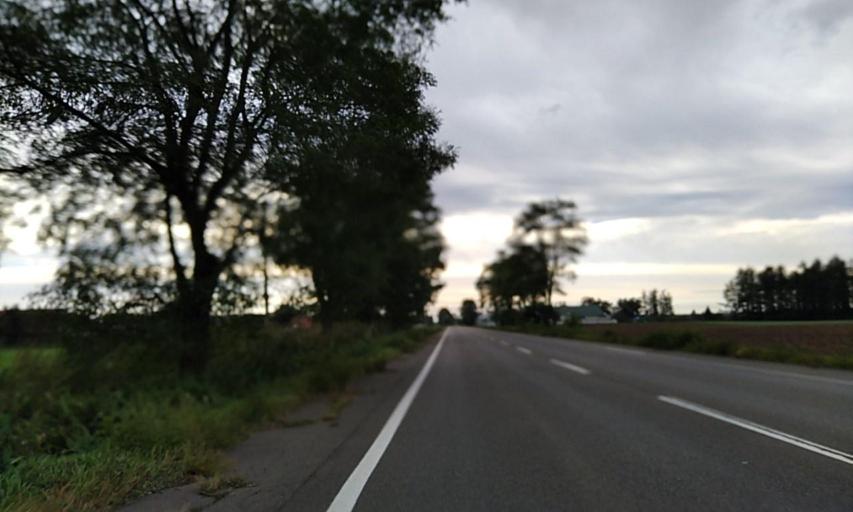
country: JP
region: Hokkaido
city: Obihiro
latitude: 42.9221
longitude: 142.9917
